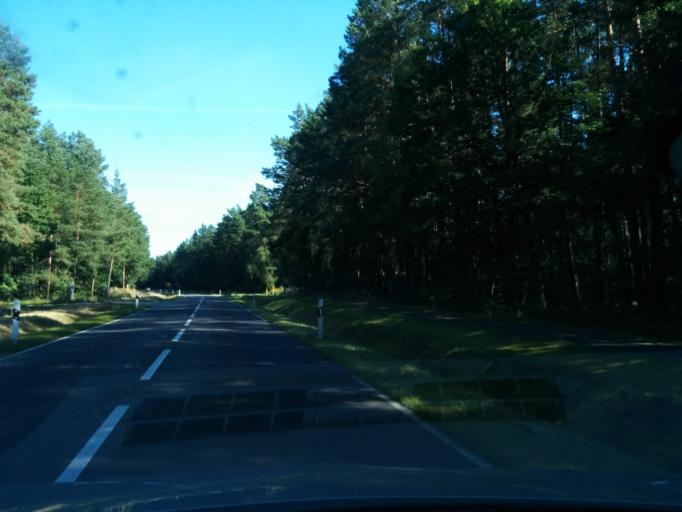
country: DE
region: Mecklenburg-Vorpommern
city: Jatznick
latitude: 53.6387
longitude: 13.9465
